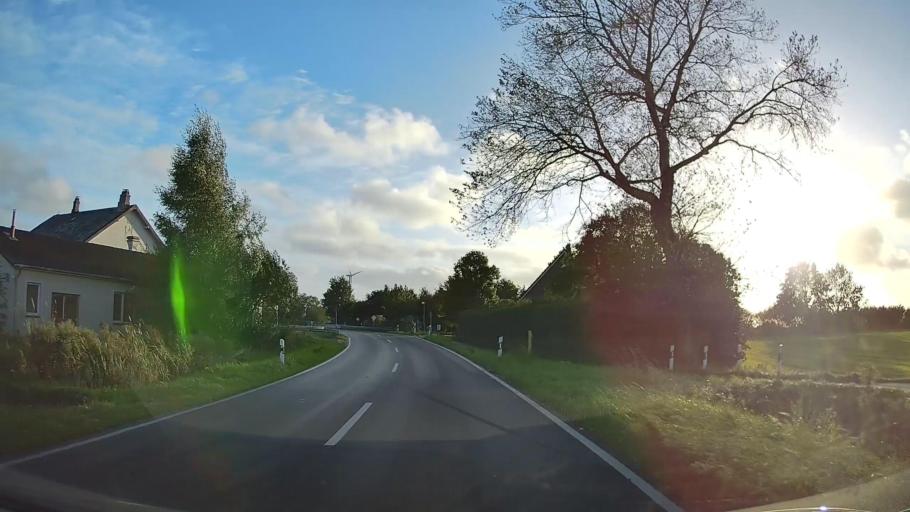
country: DE
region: Schleswig-Holstein
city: Sommerland
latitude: 53.8042
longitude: 9.5296
